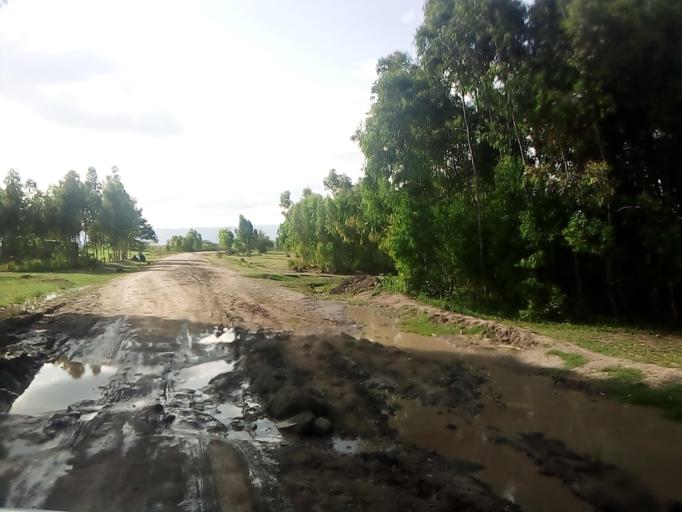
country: ET
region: Southern Nations, Nationalities, and People's Region
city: K'olito
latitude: 7.6423
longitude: 38.0545
